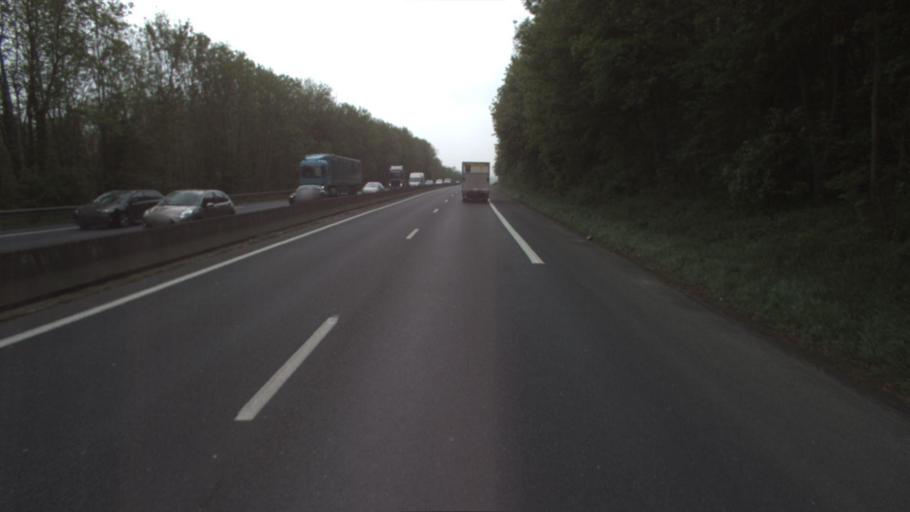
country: FR
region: Ile-de-France
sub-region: Departement de Seine-et-Marne
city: Saint-Mard
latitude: 49.0471
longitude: 2.6930
